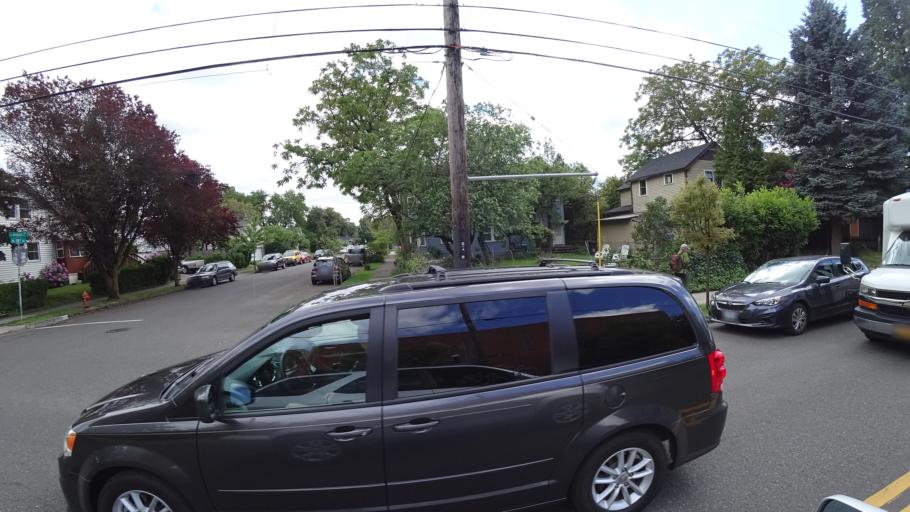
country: US
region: Oregon
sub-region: Multnomah County
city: Portland
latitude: 45.5048
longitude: -122.6477
